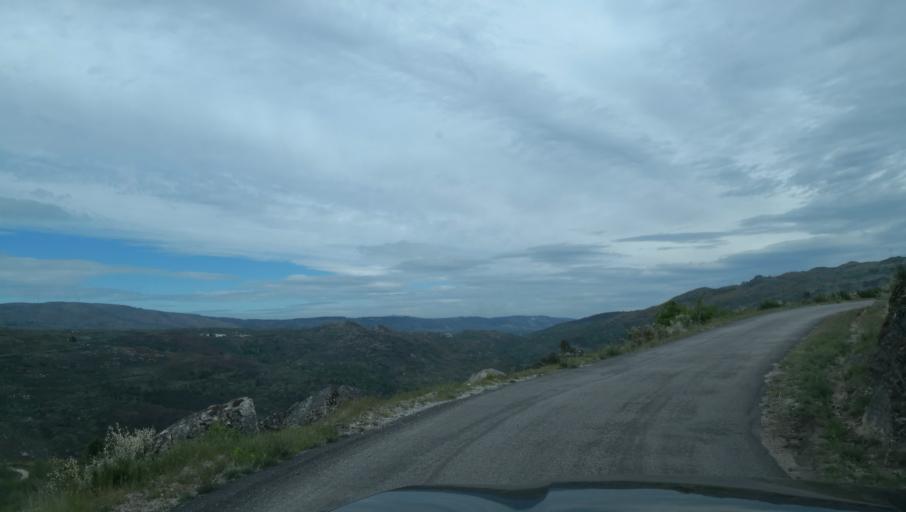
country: PT
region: Vila Real
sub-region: Vila Real
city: Vila Real
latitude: 41.3755
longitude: -7.6916
